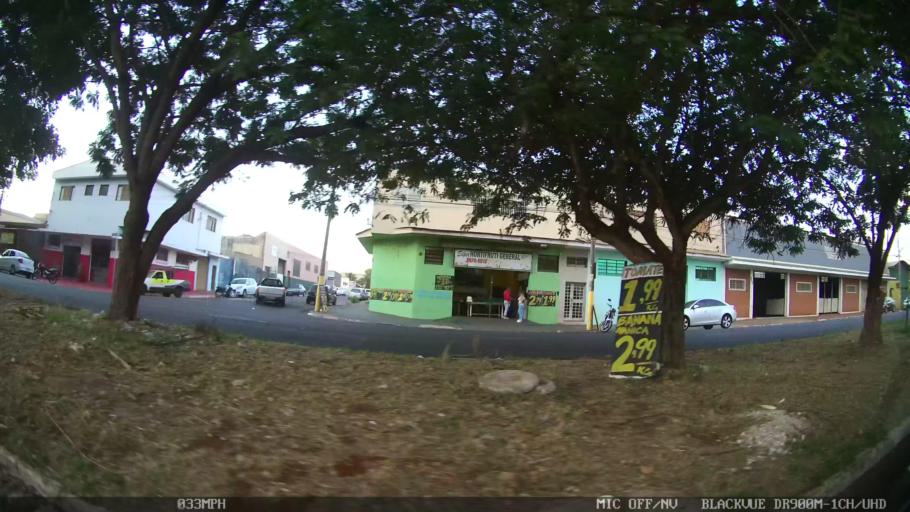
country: BR
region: Sao Paulo
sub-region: Ribeirao Preto
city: Ribeirao Preto
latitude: -21.1447
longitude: -47.7945
